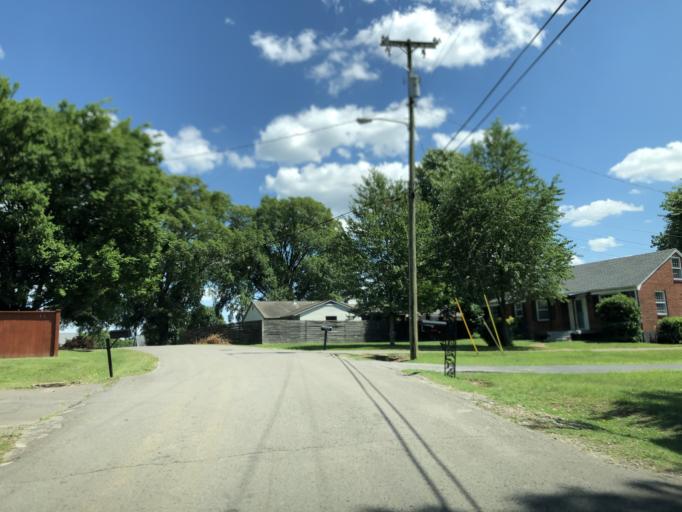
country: US
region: Tennessee
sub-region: Davidson County
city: Nashville
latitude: 36.1789
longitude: -86.7306
